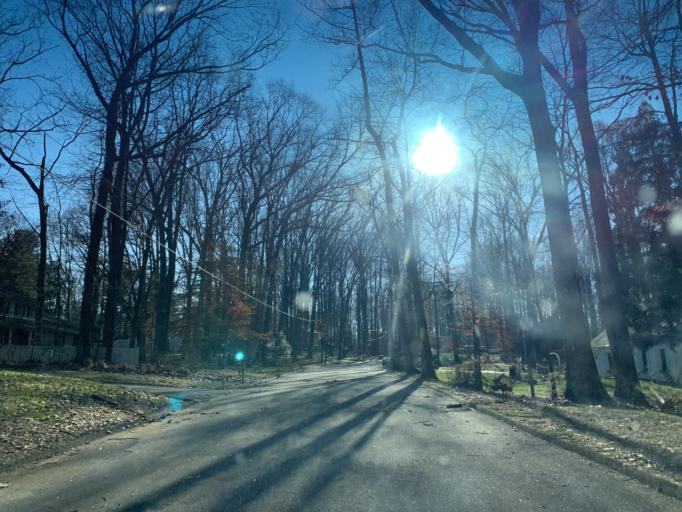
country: US
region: Maryland
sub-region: Harford County
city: South Bel Air
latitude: 39.5730
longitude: -76.2477
